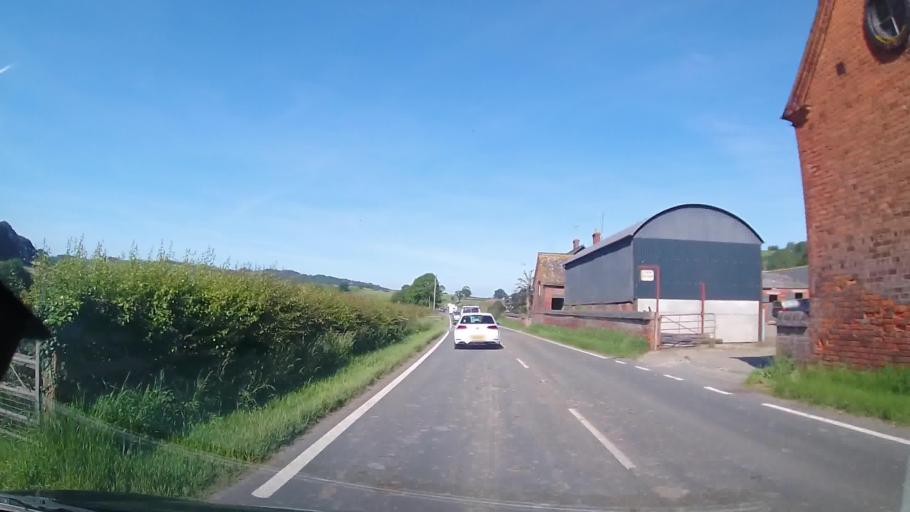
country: GB
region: Wales
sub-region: Sir Powys
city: Welshpool
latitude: 52.6500
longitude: -3.2162
